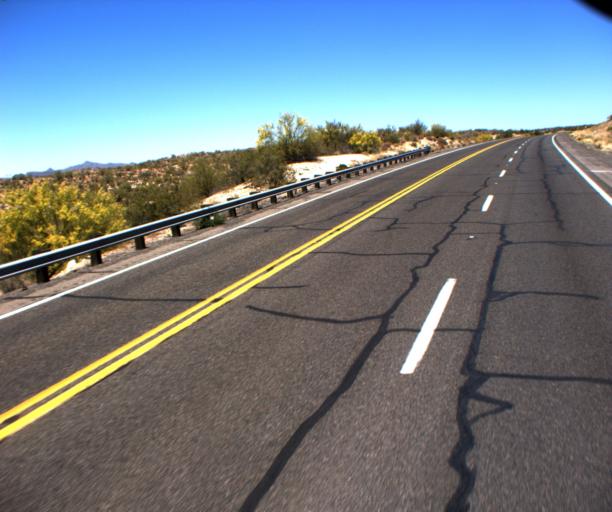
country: US
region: Arizona
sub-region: Yavapai County
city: Congress
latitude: 34.2225
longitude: -113.0691
